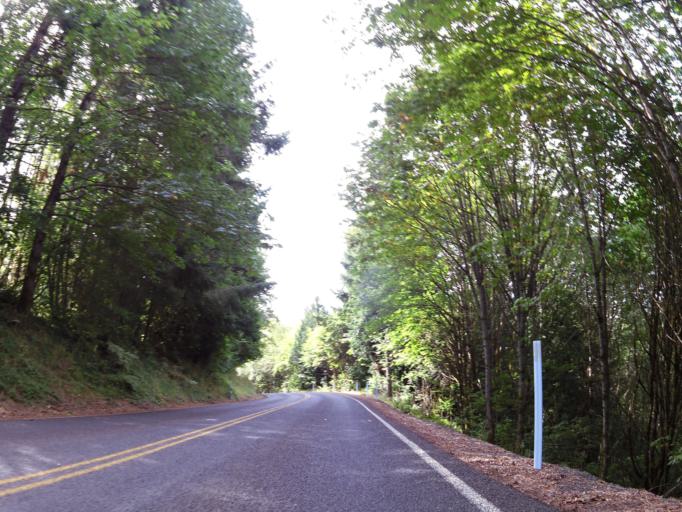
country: US
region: Washington
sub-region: Lewis County
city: Napavine
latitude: 46.5934
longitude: -122.9724
